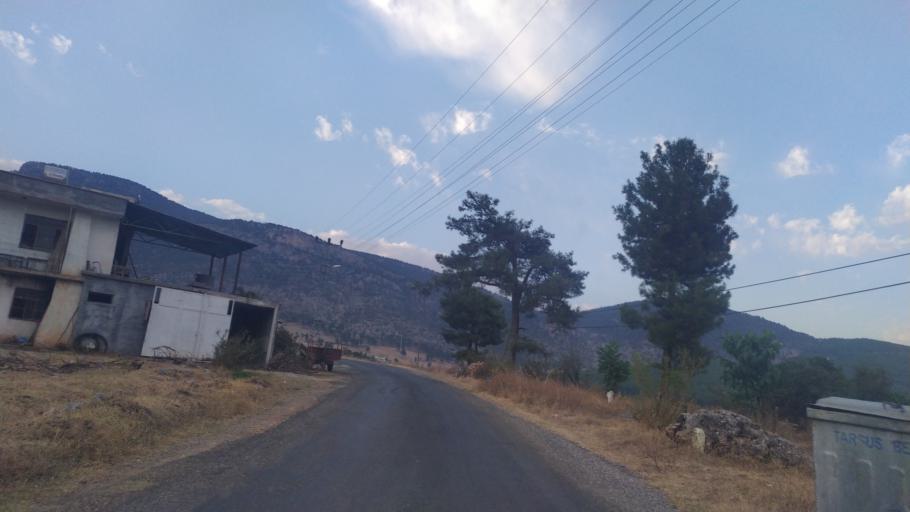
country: TR
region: Mersin
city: Camliyayla
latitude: 37.2342
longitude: 34.7178
